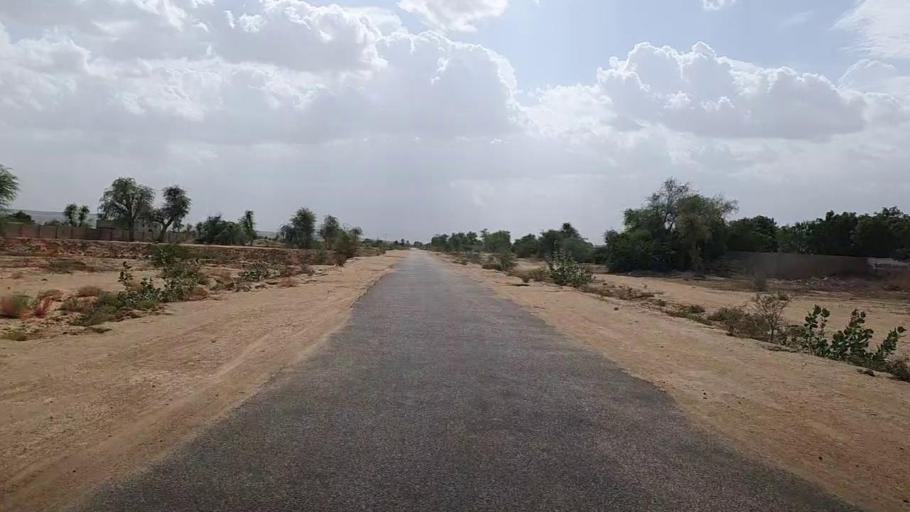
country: PK
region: Sindh
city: Jamshoro
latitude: 25.4038
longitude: 67.7857
